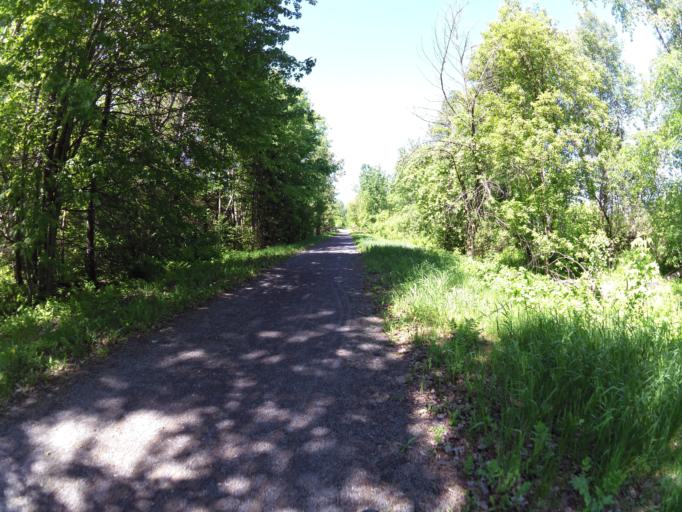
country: CA
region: Ontario
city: Clarence-Rockland
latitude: 45.4239
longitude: -75.3364
